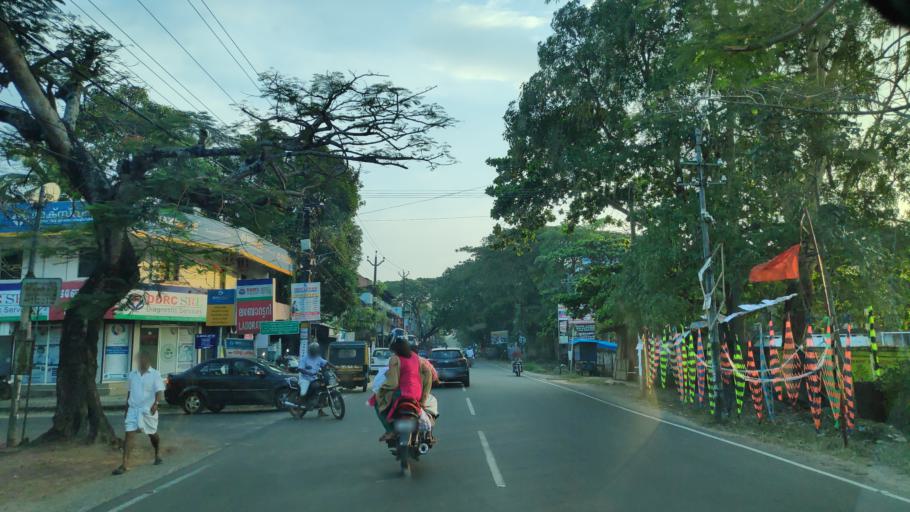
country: IN
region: Kerala
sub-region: Alappuzha
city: Shertallai
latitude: 9.6811
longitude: 76.3415
